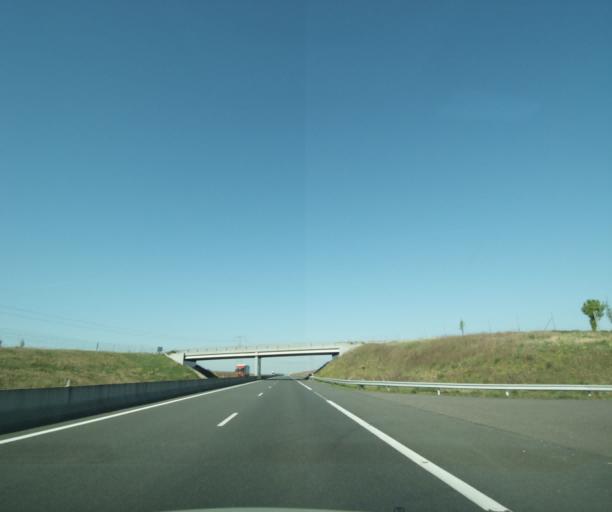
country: FR
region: Centre
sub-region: Departement du Loiret
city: Dadonville
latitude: 48.1129
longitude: 2.2497
